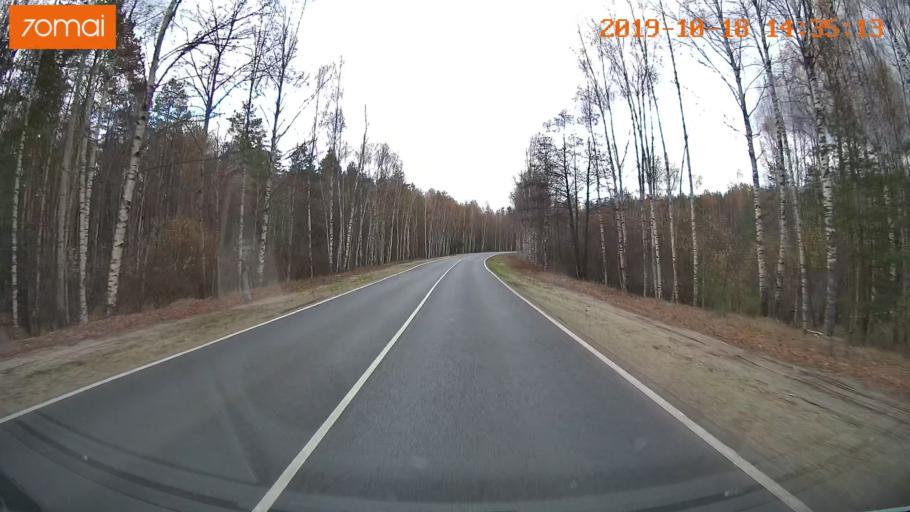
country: RU
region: Vladimir
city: Velikodvorskiy
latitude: 55.2210
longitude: 40.6322
